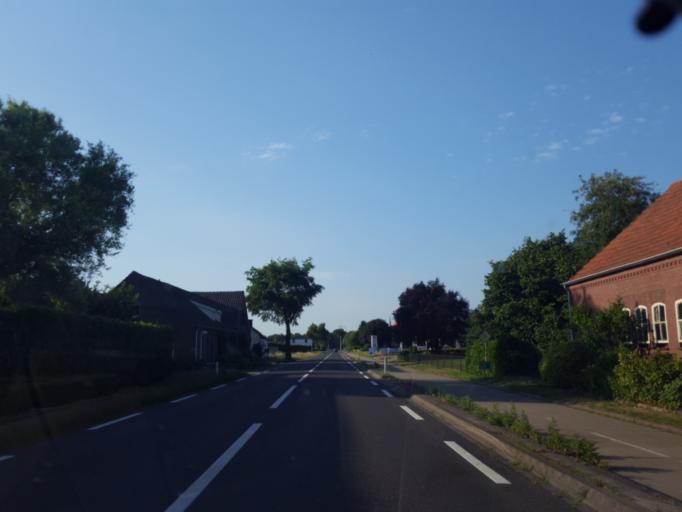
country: NL
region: Limburg
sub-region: Gemeente Leudal
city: Heythuysen
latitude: 51.3305
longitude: 5.8825
